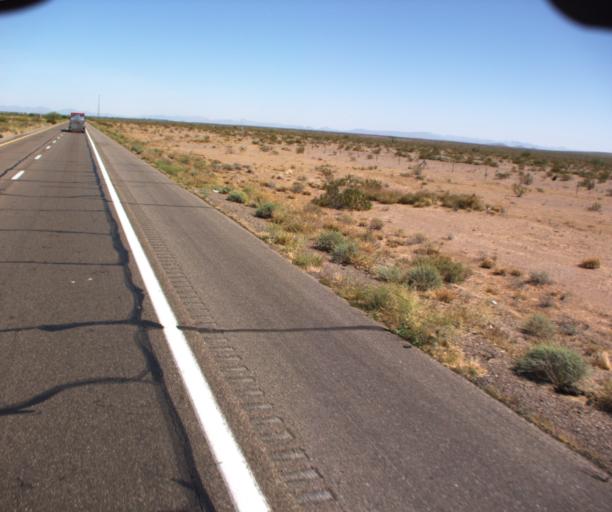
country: US
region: Arizona
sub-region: Maricopa County
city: Gila Bend
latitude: 32.9012
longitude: -113.0060
